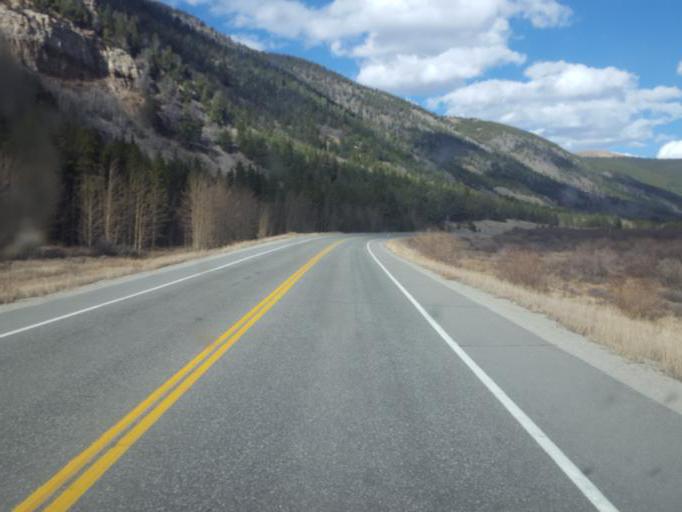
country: US
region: Colorado
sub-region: Lake County
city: Leadville North
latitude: 39.2932
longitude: -106.2758
